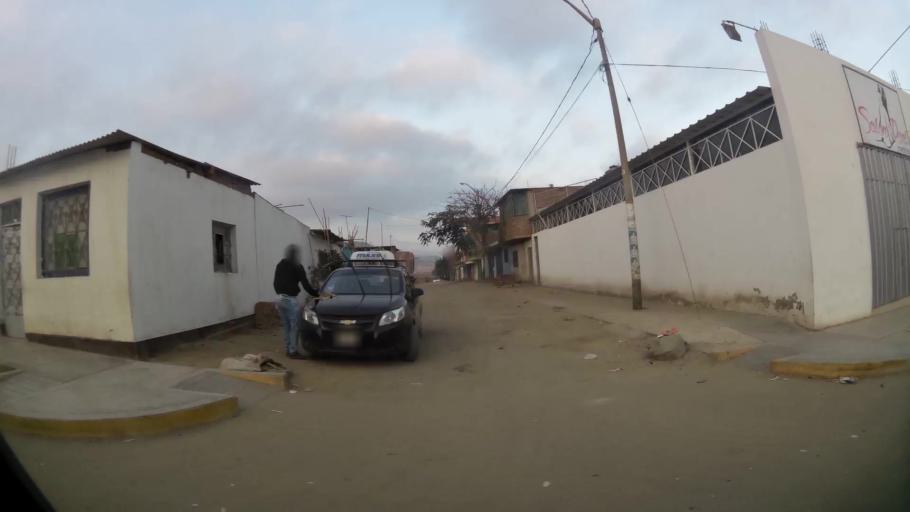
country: PE
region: La Libertad
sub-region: Provincia de Trujillo
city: El Porvenir
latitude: -8.0651
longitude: -79.0071
